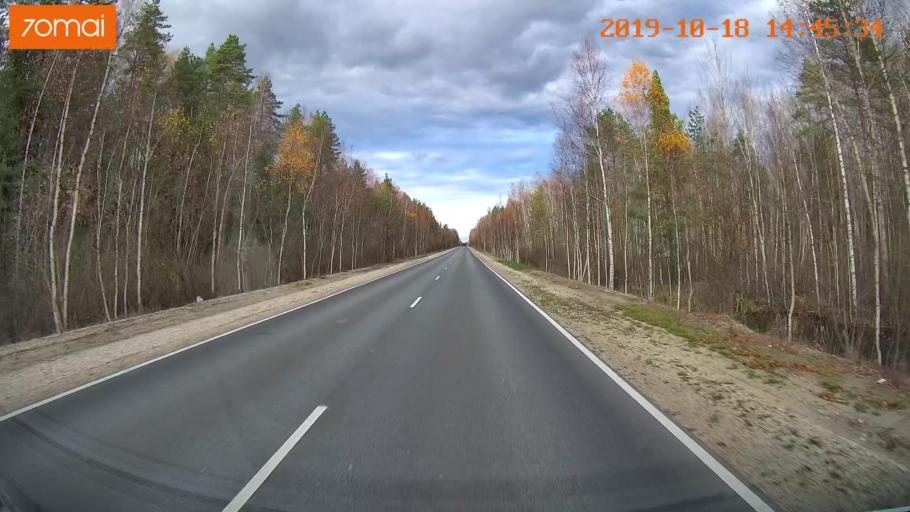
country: RU
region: Vladimir
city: Velikodvorskiy
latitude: 55.3571
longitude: 40.6794
